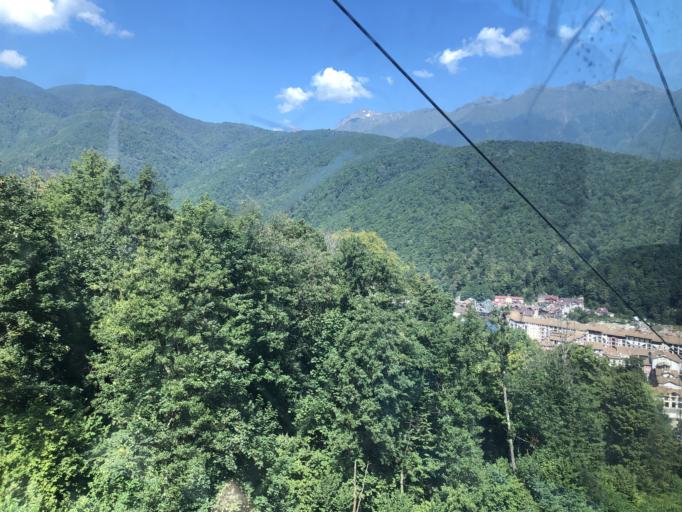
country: RU
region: Krasnodarskiy
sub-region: Sochi City
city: Krasnaya Polyana
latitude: 43.6787
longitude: 40.2644
